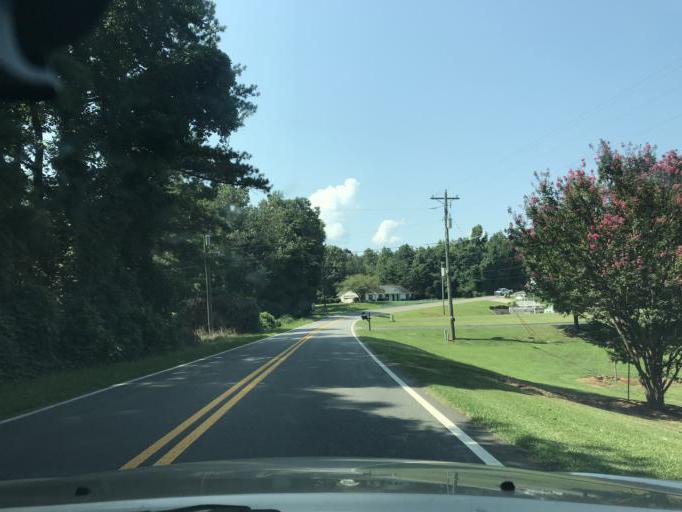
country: US
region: Georgia
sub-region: Hall County
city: Flowery Branch
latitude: 34.2339
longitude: -83.9973
